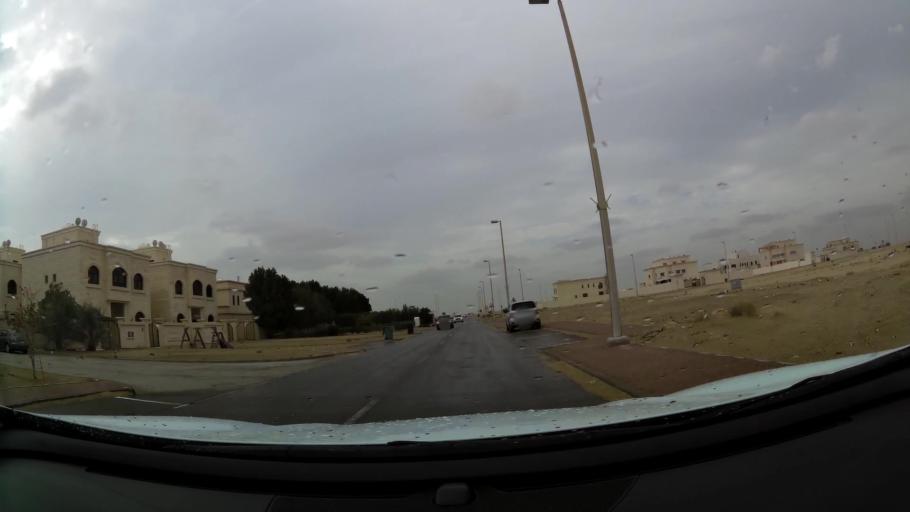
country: AE
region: Abu Dhabi
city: Abu Dhabi
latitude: 24.3617
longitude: 54.6206
